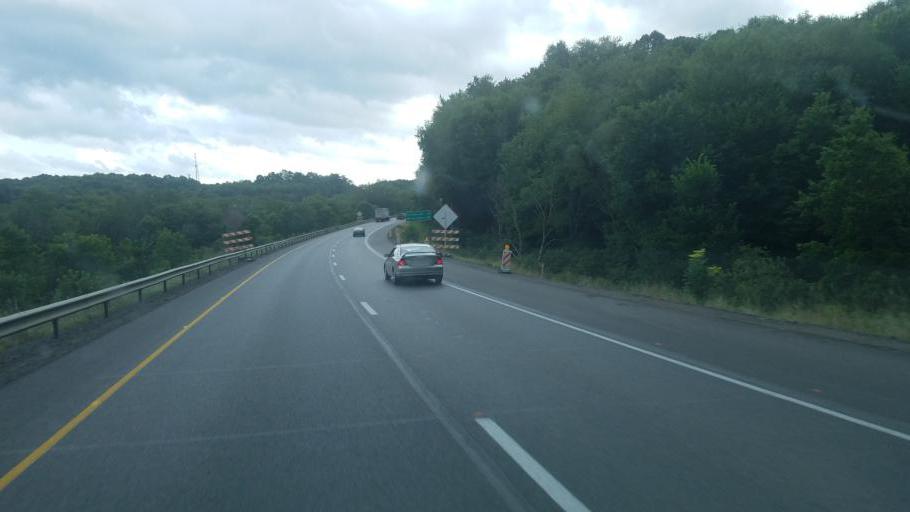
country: US
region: Pennsylvania
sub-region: Butler County
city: Evans City
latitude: 40.7497
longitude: -80.1076
